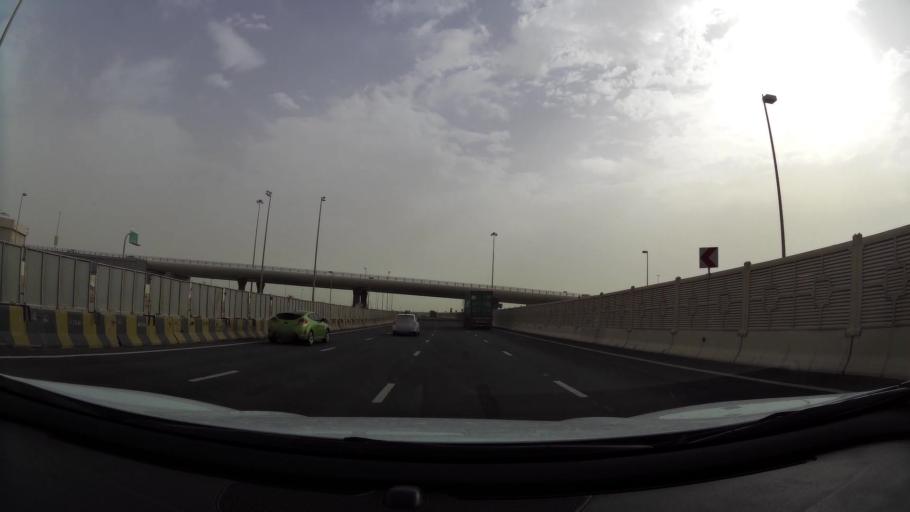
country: AE
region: Abu Dhabi
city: Abu Dhabi
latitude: 24.4491
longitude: 54.6151
